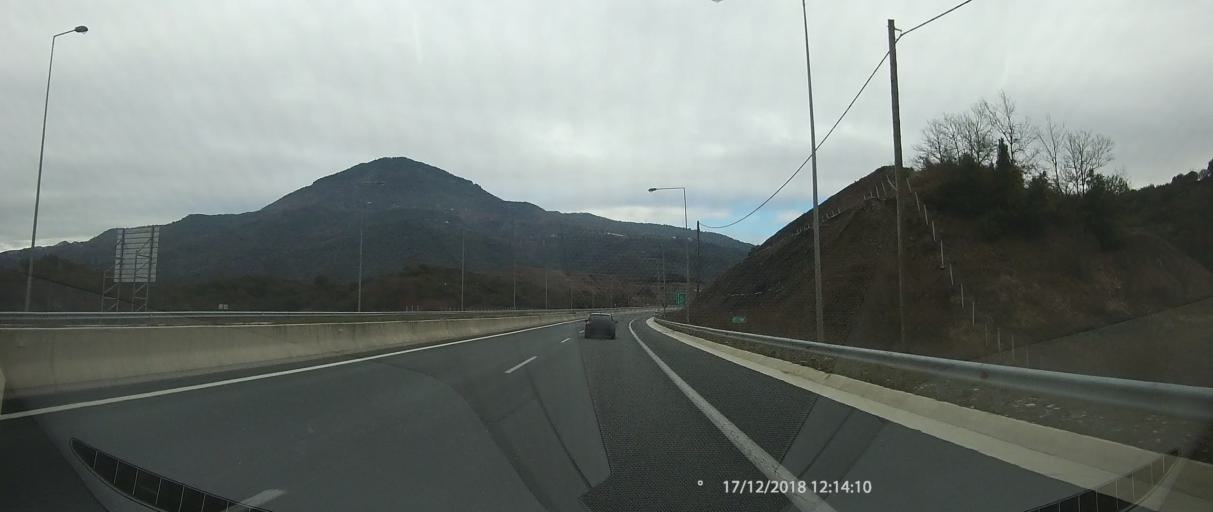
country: GR
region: Epirus
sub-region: Nomos Ioanninon
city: Katsikas
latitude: 39.7160
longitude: 20.9901
